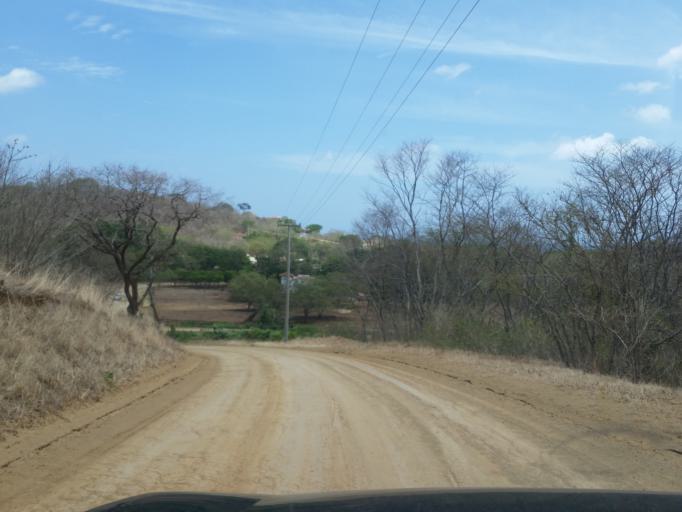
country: NI
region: Rivas
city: Tola
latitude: 11.4446
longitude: -86.0805
